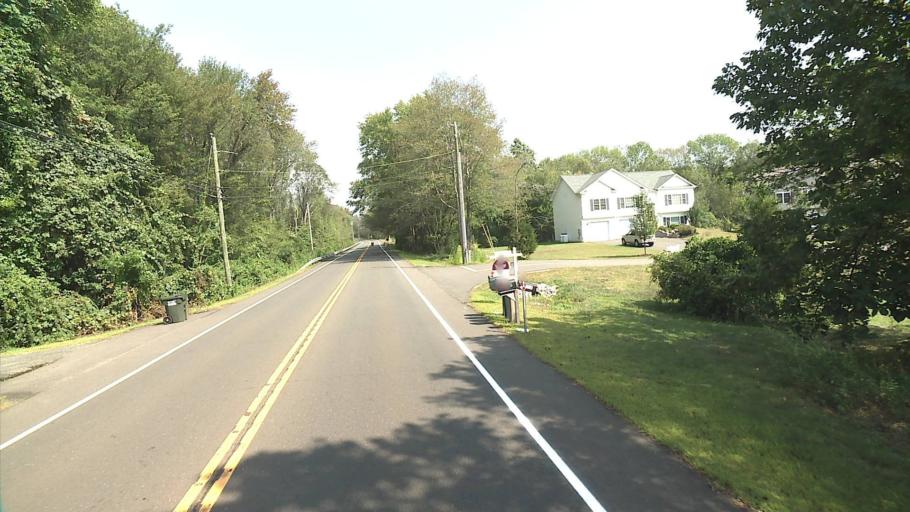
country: US
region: Connecticut
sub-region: Middlesex County
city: Durham
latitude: 41.4251
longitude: -72.6511
